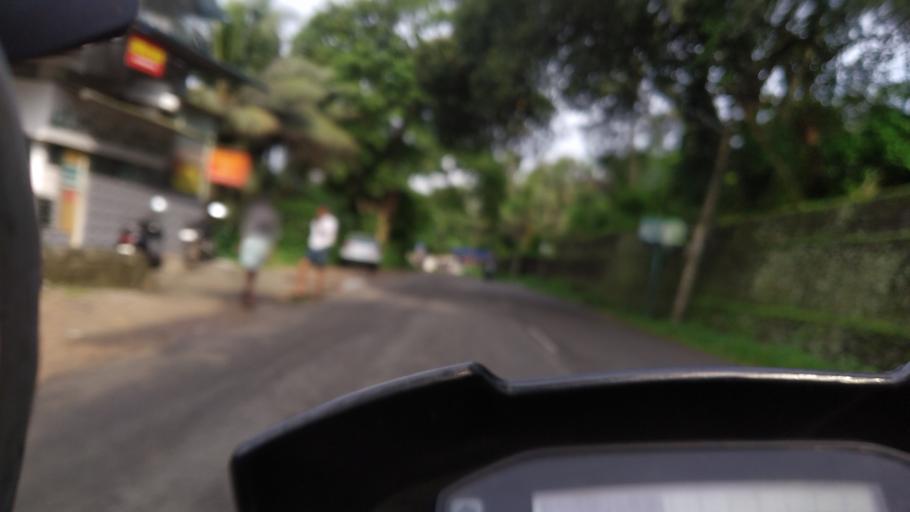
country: IN
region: Kerala
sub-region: Ernakulam
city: Kotamangalam
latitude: 10.0497
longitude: 76.7181
